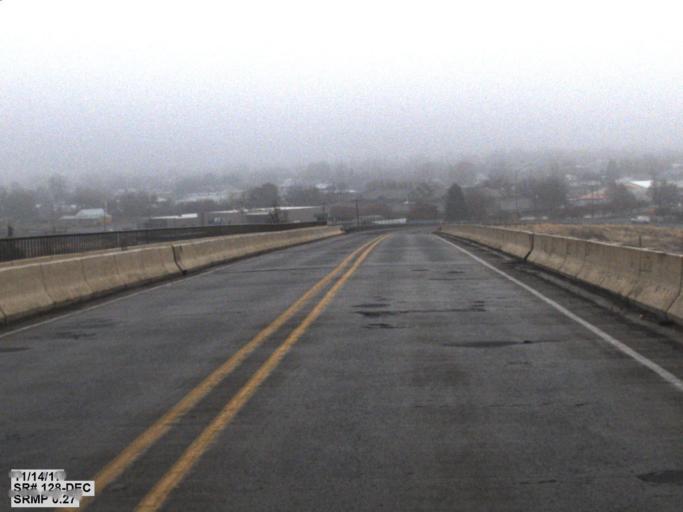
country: US
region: Washington
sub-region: Asotin County
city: West Clarkston-Highland
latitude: 46.4238
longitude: -117.0712
